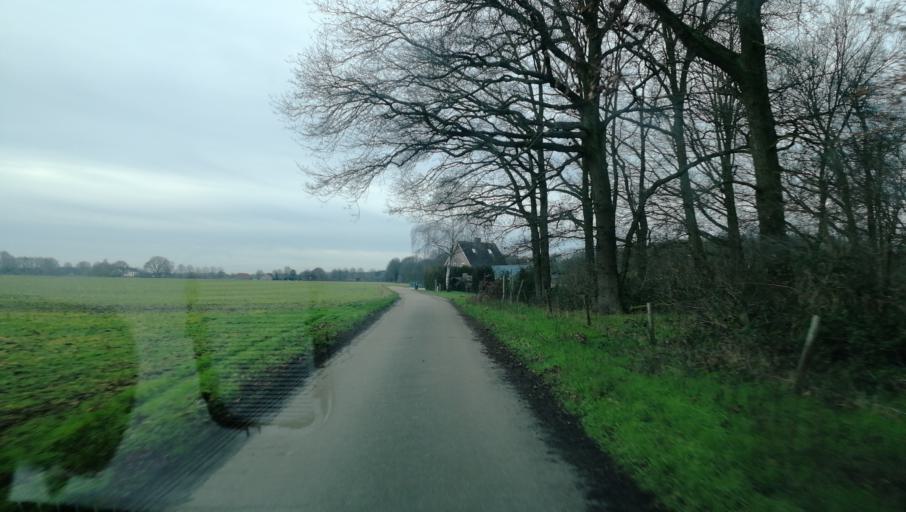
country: NL
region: Limburg
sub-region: Gemeente Venlo
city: Arcen
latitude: 51.4311
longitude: 6.1907
